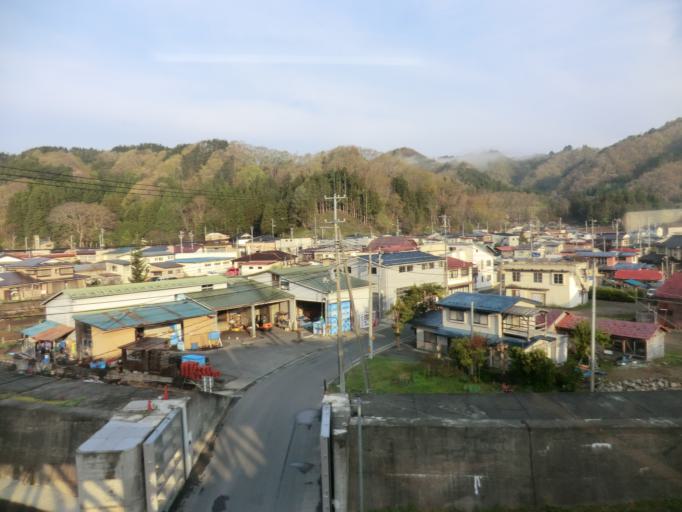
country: JP
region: Iwate
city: Miyako
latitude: 40.0079
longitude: 141.8876
